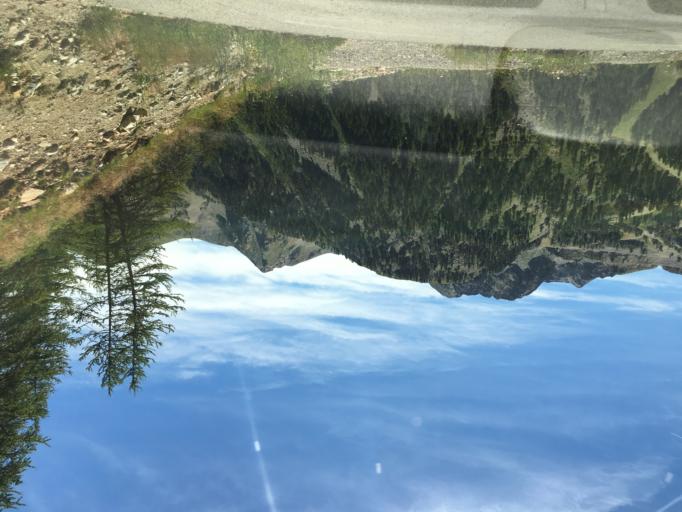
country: IT
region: Piedmont
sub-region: Provincia di Cuneo
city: Vinadio
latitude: 44.1943
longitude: 7.1545
